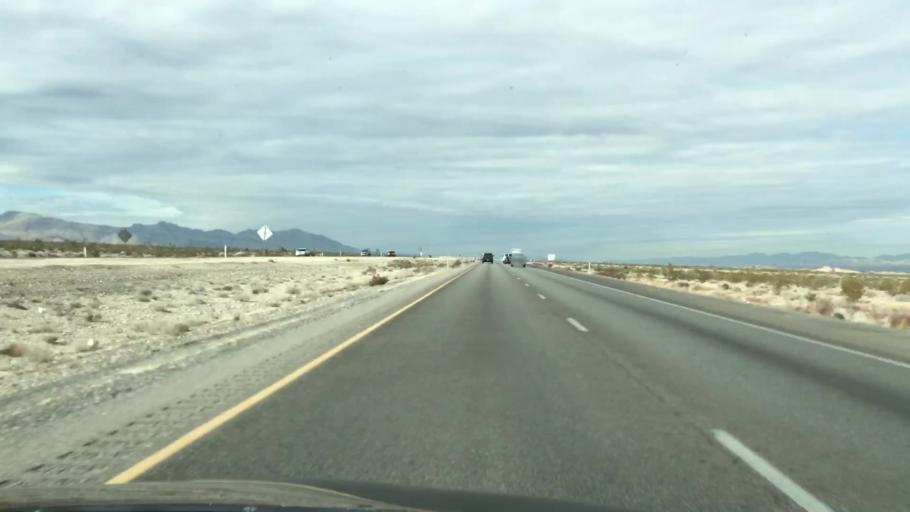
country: US
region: Nevada
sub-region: Clark County
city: Summerlin South
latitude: 36.3421
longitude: -115.3268
